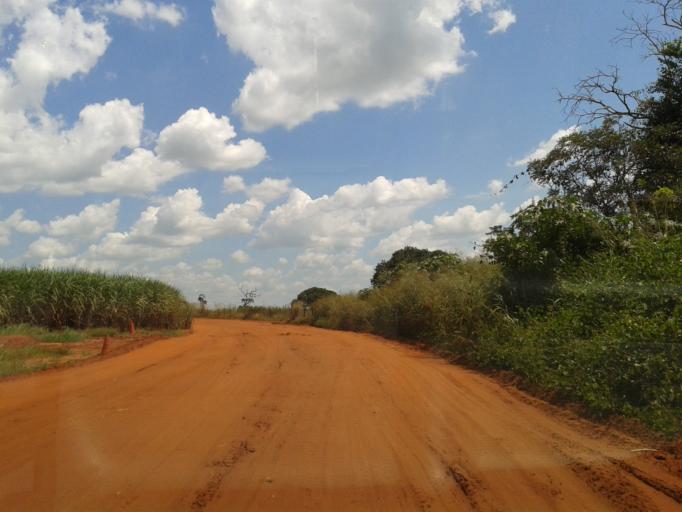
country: BR
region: Minas Gerais
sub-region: Ituiutaba
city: Ituiutaba
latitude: -19.0436
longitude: -49.7100
